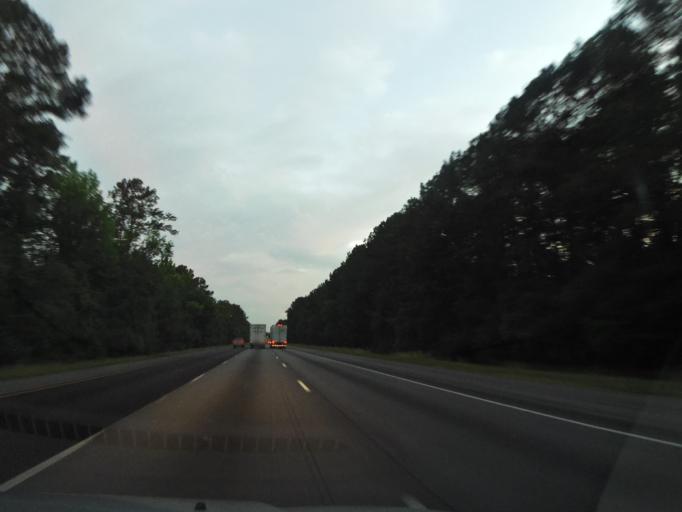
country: US
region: Georgia
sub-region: Bryan County
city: Richmond Hill
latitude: 31.8796
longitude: -81.3304
